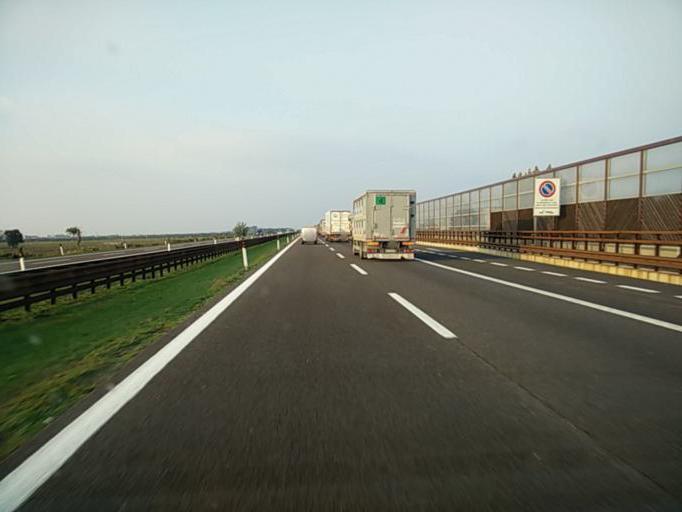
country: IT
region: Veneto
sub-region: Provincia di Verona
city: Forette
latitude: 45.3419
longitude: 10.9185
